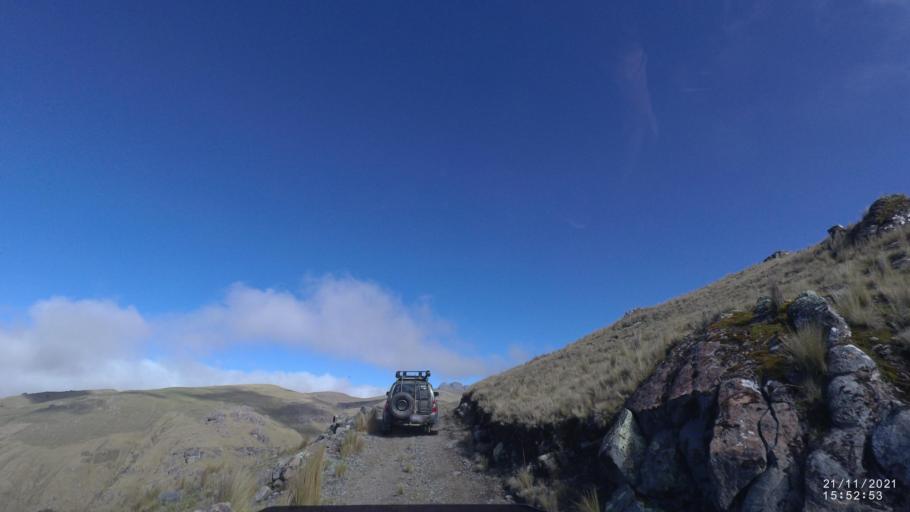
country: BO
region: Cochabamba
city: Cochabamba
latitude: -16.9706
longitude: -66.2679
